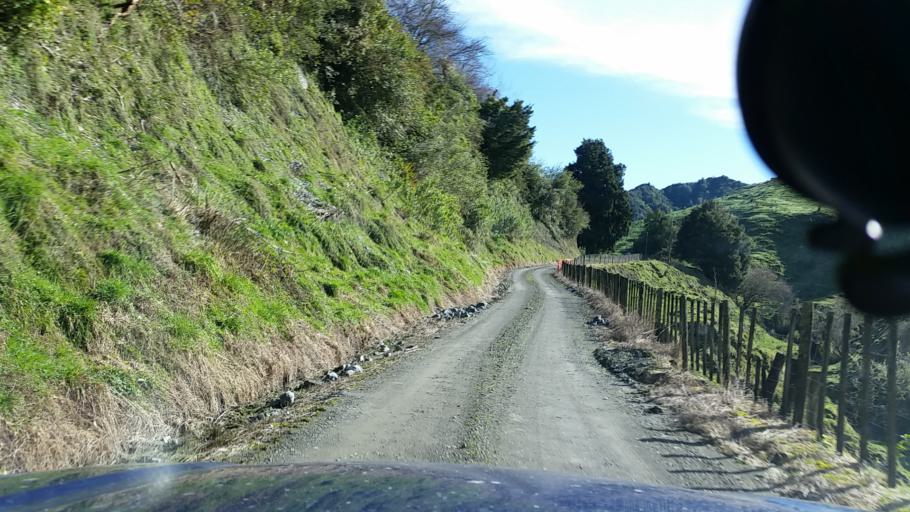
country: NZ
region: Taranaki
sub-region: New Plymouth District
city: Waitara
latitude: -39.0531
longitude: 174.7528
